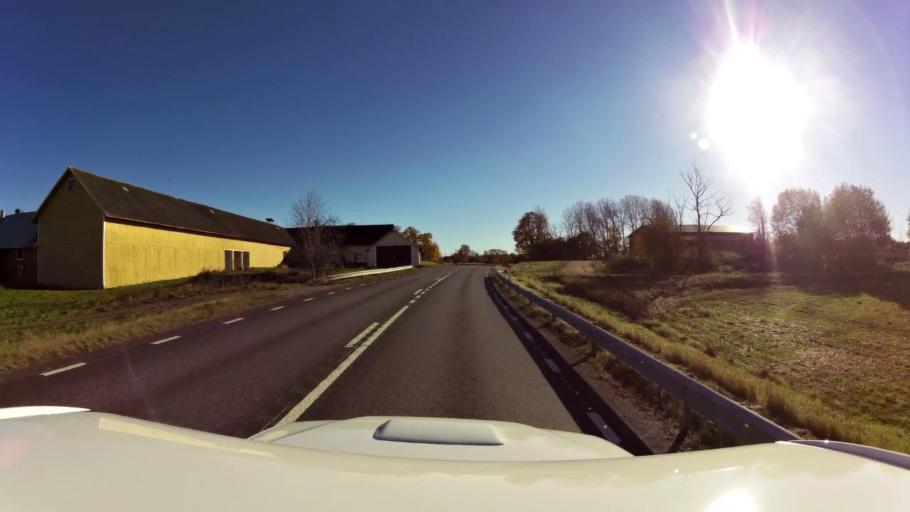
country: SE
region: OEstergoetland
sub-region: Linkopings Kommun
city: Ljungsbro
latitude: 58.5288
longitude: 15.4073
